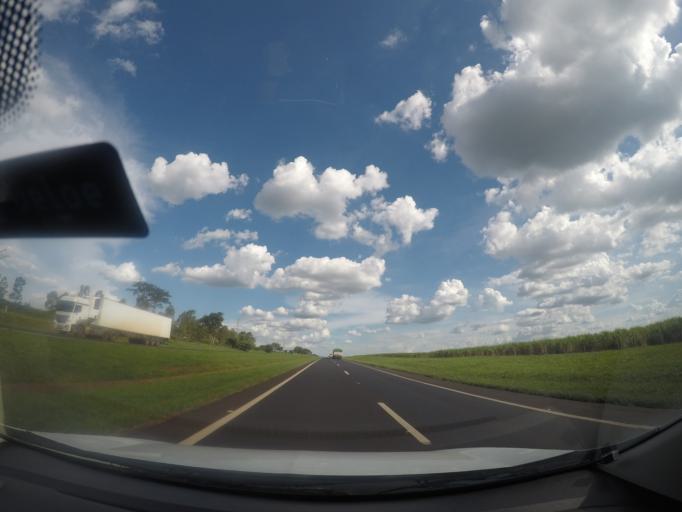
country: BR
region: Sao Paulo
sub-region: Bebedouro
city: Bebedouro
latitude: -20.8579
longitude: -48.4769
